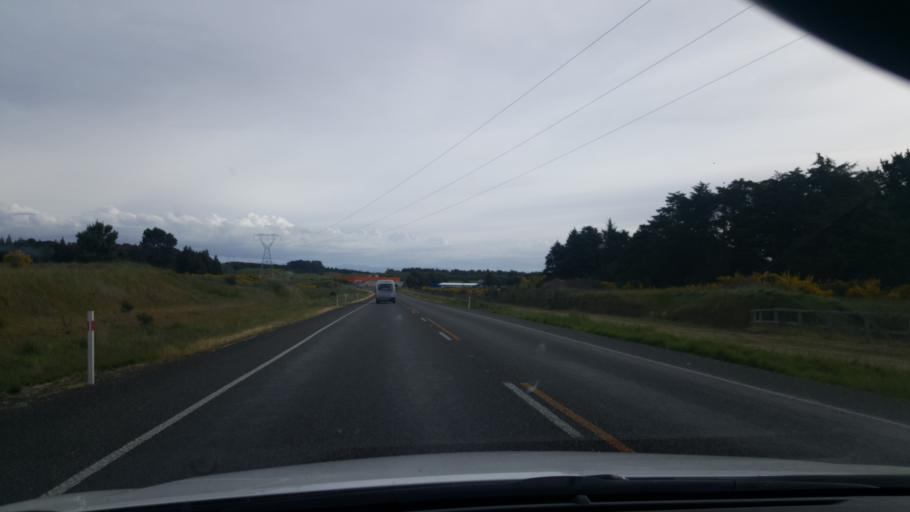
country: NZ
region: Waikato
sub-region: Taupo District
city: Taupo
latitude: -38.6963
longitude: 176.1132
